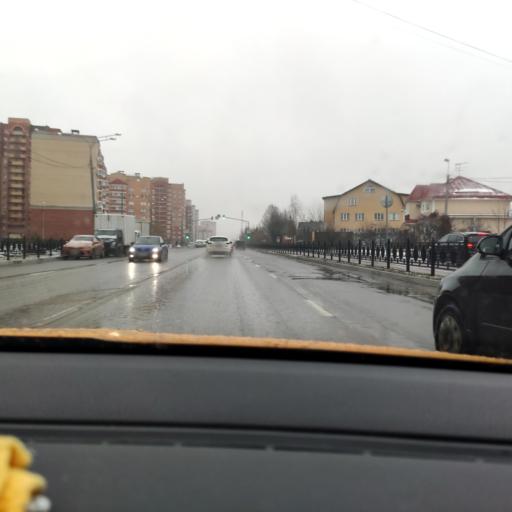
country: RU
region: Moskovskaya
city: Domodedovo
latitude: 55.4284
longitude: 37.7539
